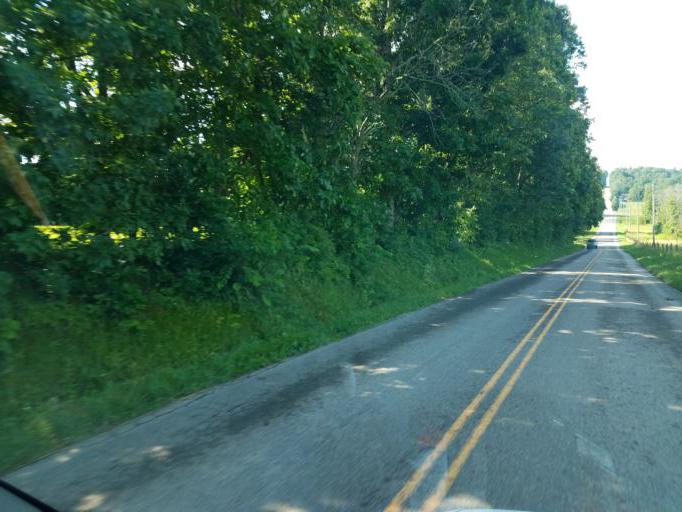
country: US
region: Ohio
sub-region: Knox County
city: Danville
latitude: 40.5298
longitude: -82.3608
